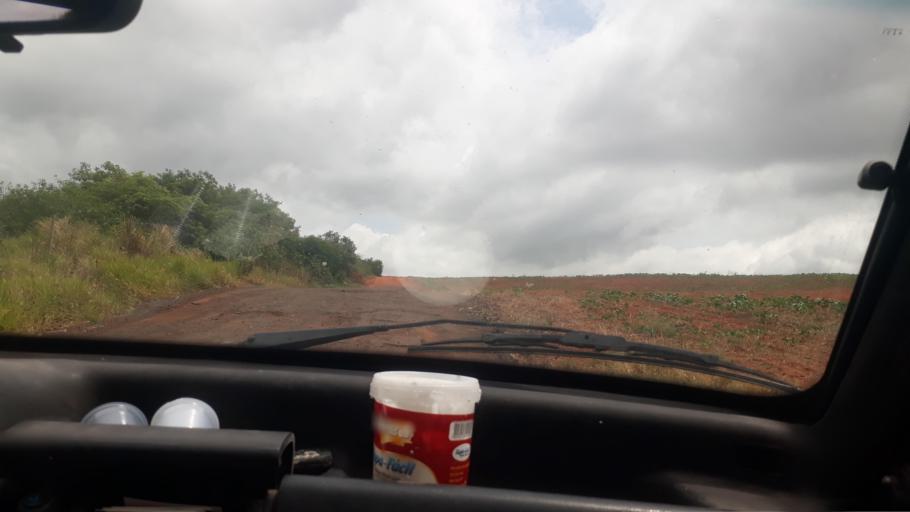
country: BR
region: Sao Paulo
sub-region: Regente Feijo
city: Regente Feijo
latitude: -22.2639
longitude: -51.3027
